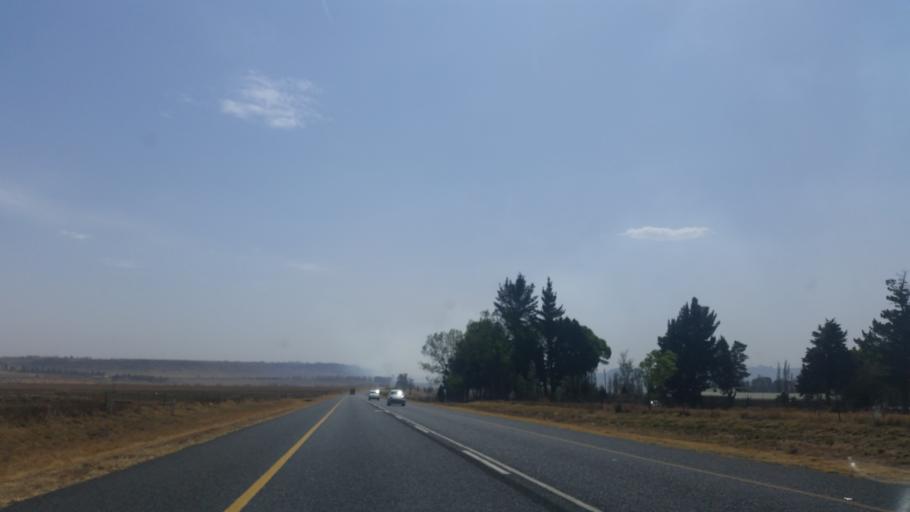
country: ZA
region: Orange Free State
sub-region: Thabo Mofutsanyana District Municipality
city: Bethlehem
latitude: -28.2815
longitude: 28.3911
